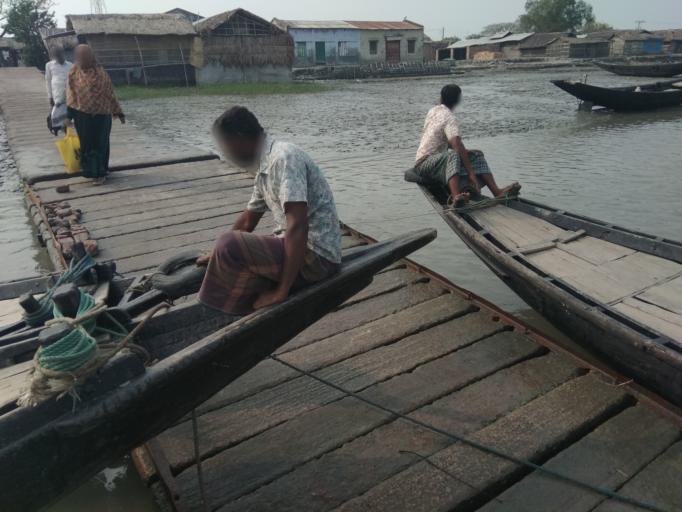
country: IN
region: West Bengal
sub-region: North 24 Parganas
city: Taki
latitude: 22.3473
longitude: 89.2038
